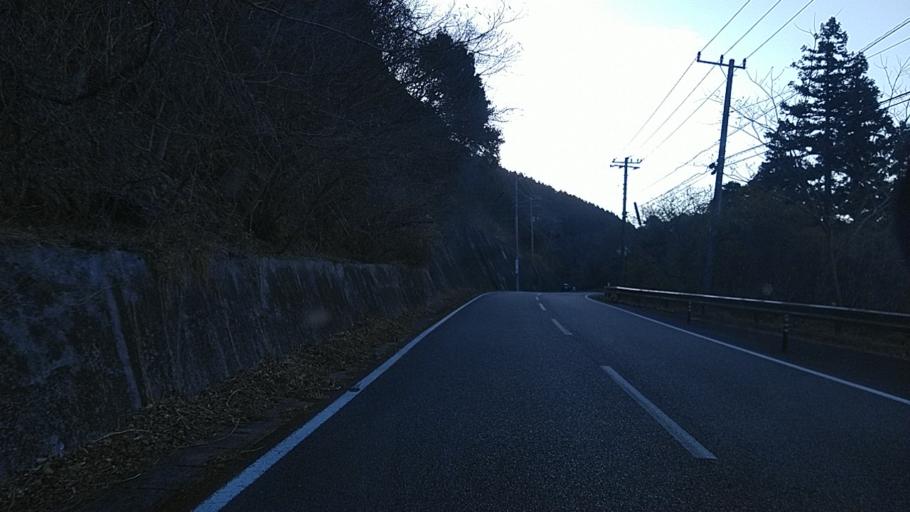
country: JP
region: Chiba
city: Kimitsu
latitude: 35.2614
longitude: 139.9326
